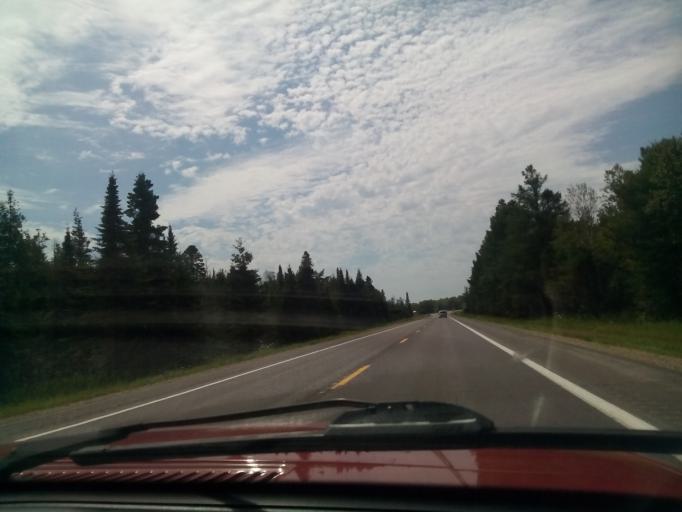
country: US
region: Michigan
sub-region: Schoolcraft County
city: Manistique
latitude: 46.0016
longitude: -86.0018
